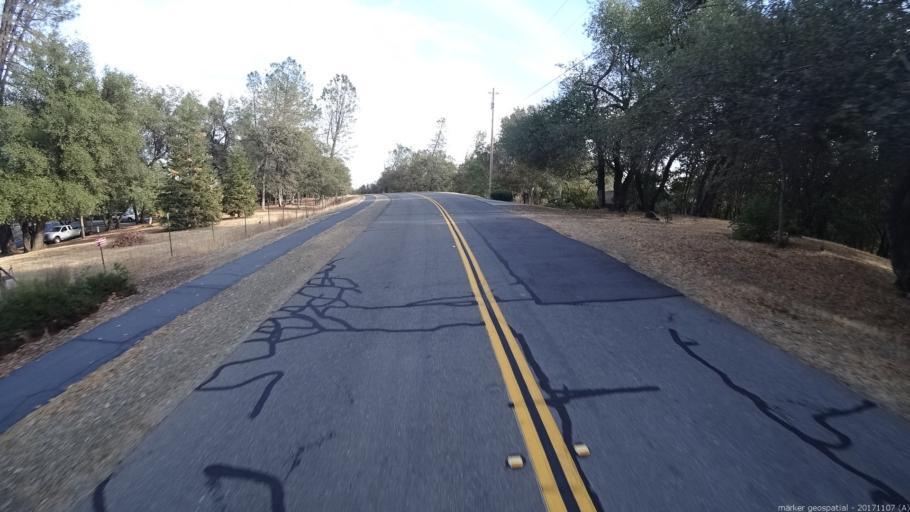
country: US
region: California
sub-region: Shasta County
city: Shasta
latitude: 40.5199
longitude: -122.4648
